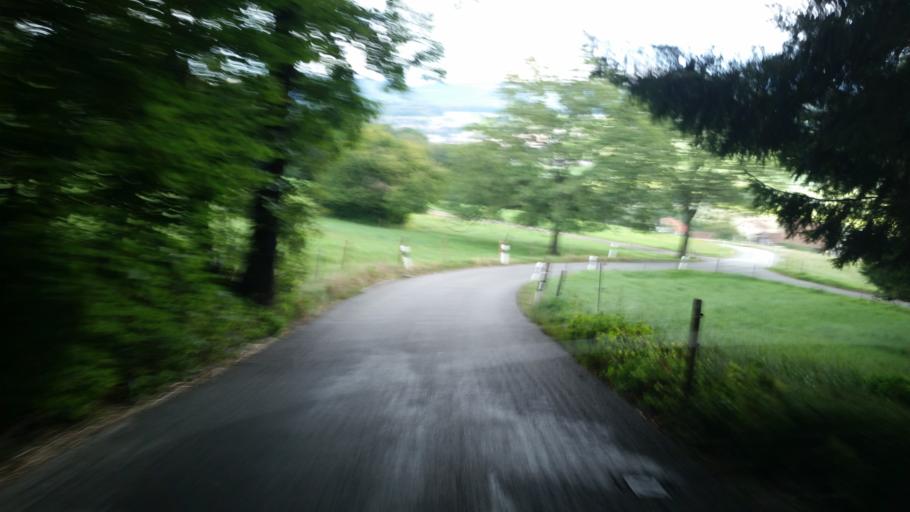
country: CH
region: Zurich
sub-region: Bezirk Affoltern
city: Hedingen
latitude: 47.3192
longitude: 8.4443
